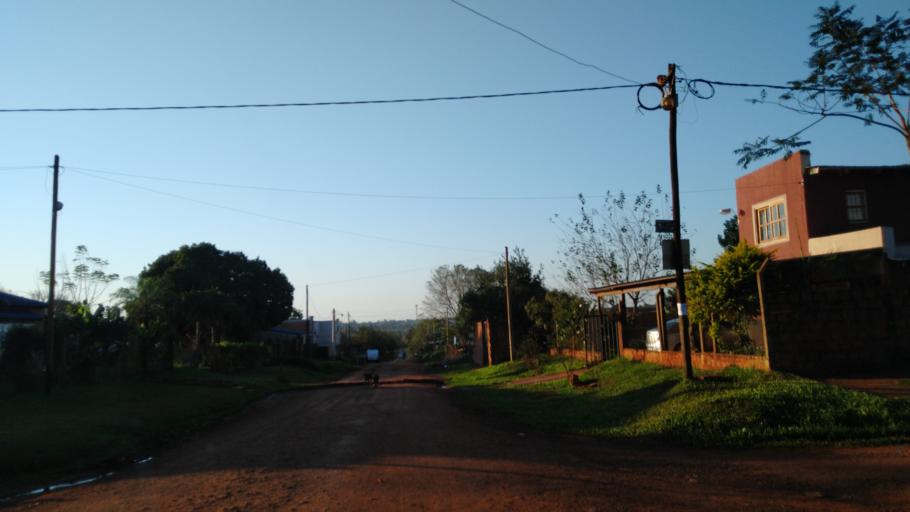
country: AR
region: Misiones
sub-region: Departamento de Capital
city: Posadas
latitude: -27.4258
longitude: -55.9211
